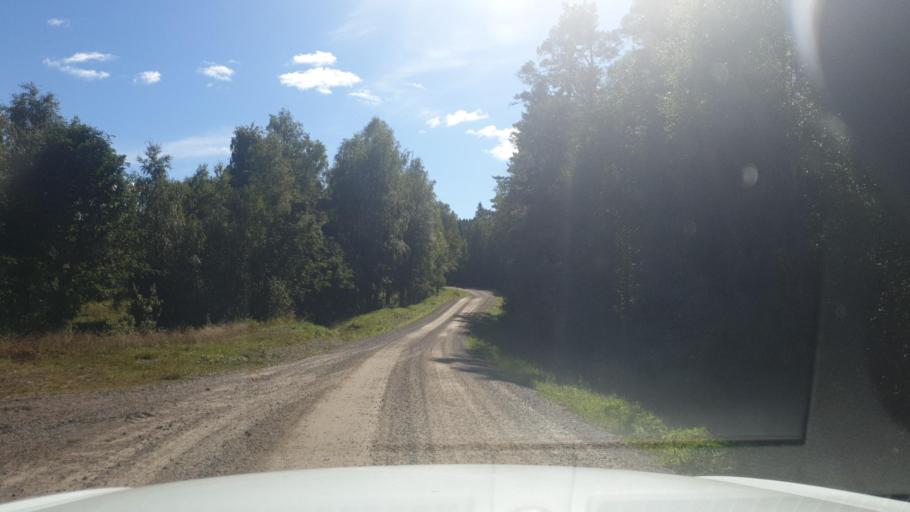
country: SE
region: Vaermland
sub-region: Eda Kommun
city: Charlottenberg
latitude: 60.0721
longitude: 12.5304
